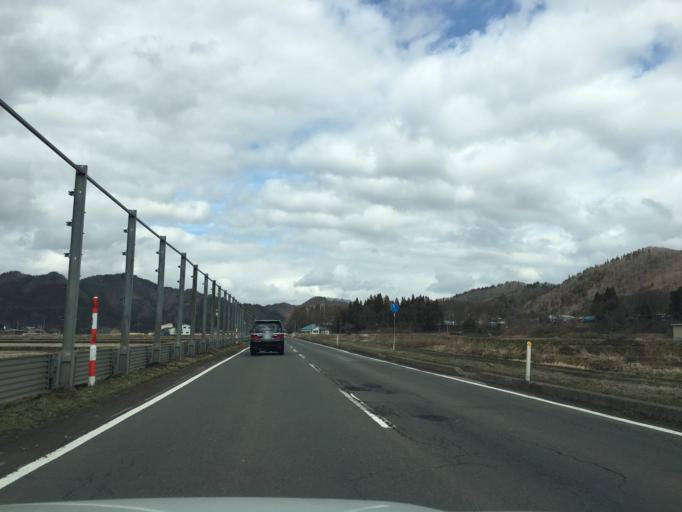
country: JP
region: Akita
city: Hanawa
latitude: 40.2322
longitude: 140.7335
